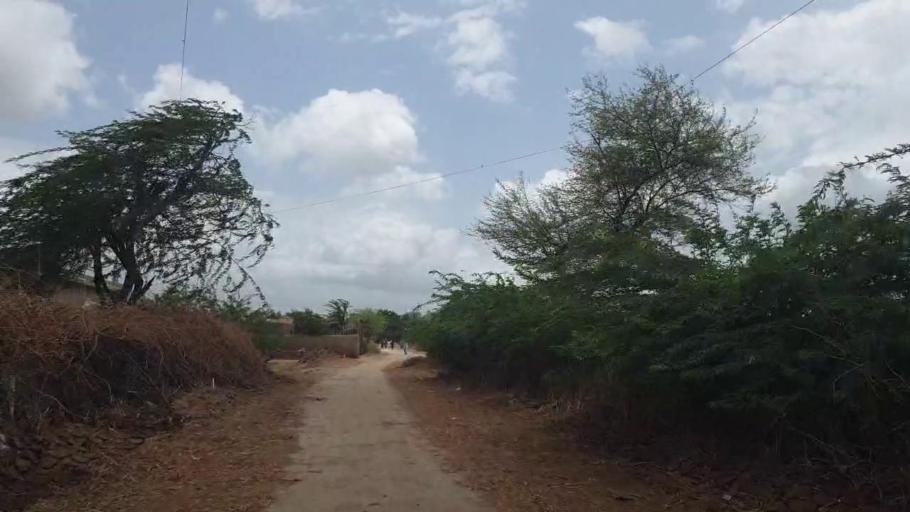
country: PK
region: Sindh
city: Badin
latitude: 24.6472
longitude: 68.9210
